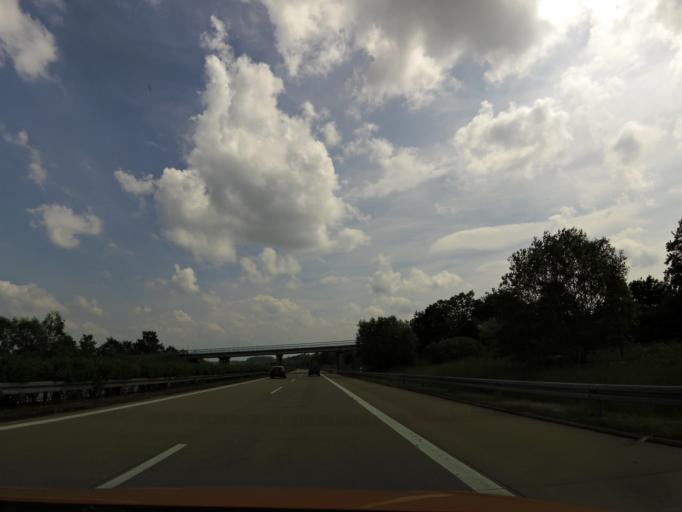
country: DE
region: Mecklenburg-Vorpommern
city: Siggelkow
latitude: 53.3132
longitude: 11.9026
